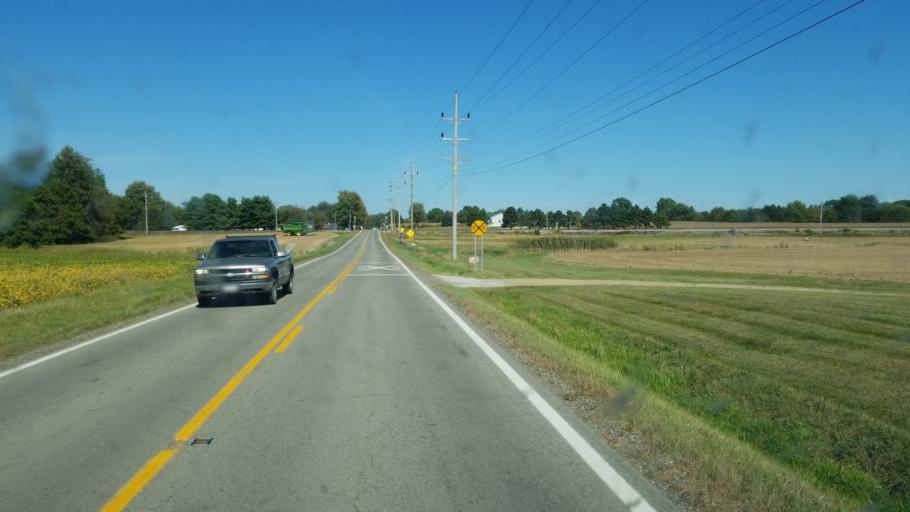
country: US
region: Ohio
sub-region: Huron County
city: Plymouth
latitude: 41.0208
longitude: -82.6875
